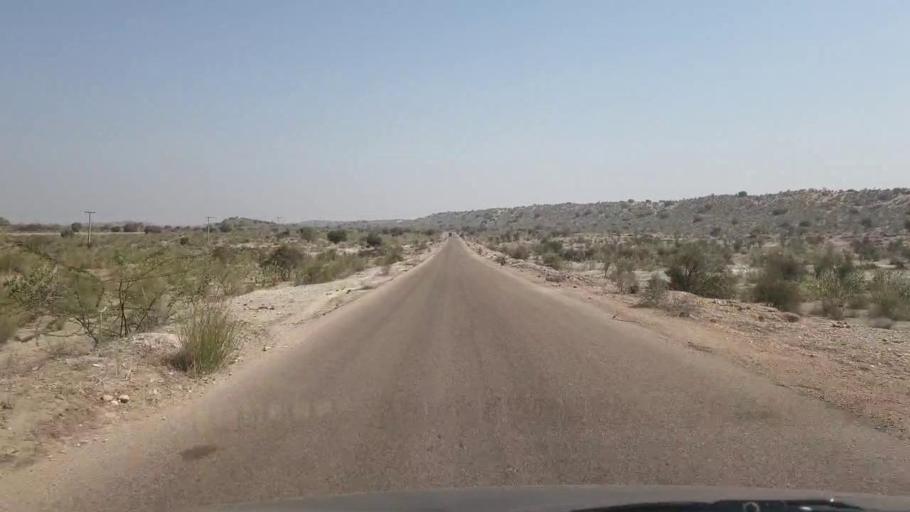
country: PK
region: Sindh
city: Chor
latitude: 25.6075
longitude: 70.0345
